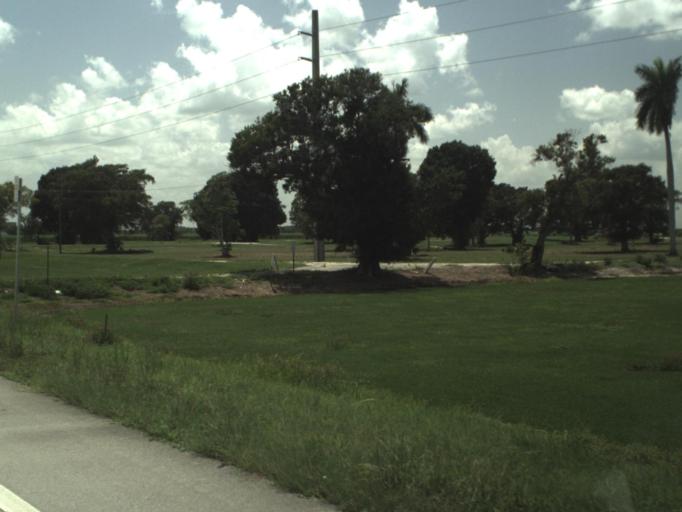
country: US
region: Florida
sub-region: Palm Beach County
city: Belle Glade
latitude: 26.7145
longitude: -80.6682
